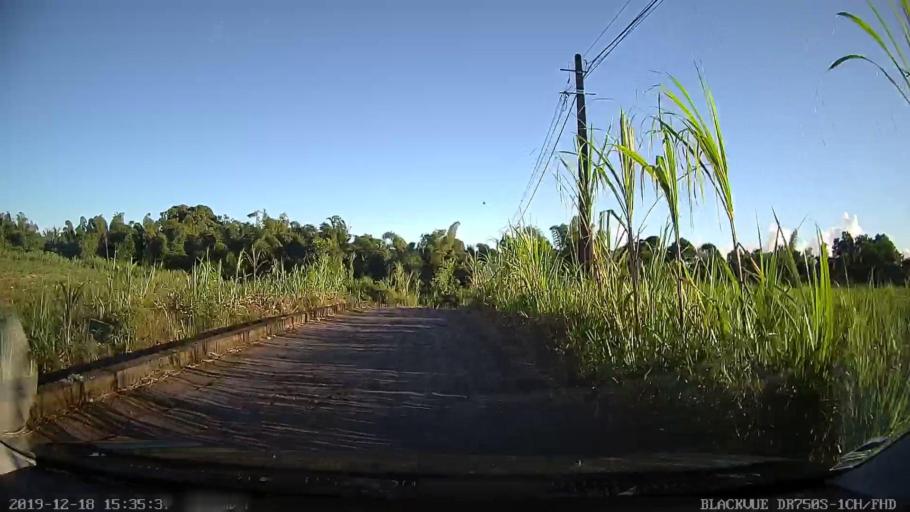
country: RE
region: Reunion
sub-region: Reunion
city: Bras-Panon
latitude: -20.9971
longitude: 55.6626
